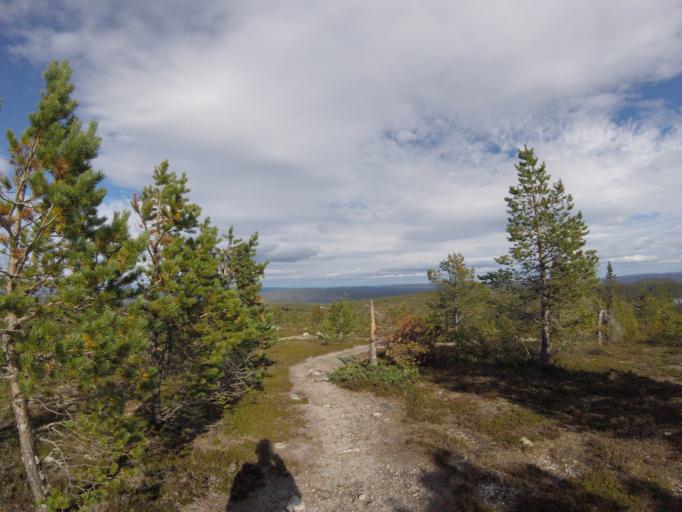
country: NO
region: Buskerud
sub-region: Flesberg
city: Lampeland
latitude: 59.7604
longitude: 9.4296
